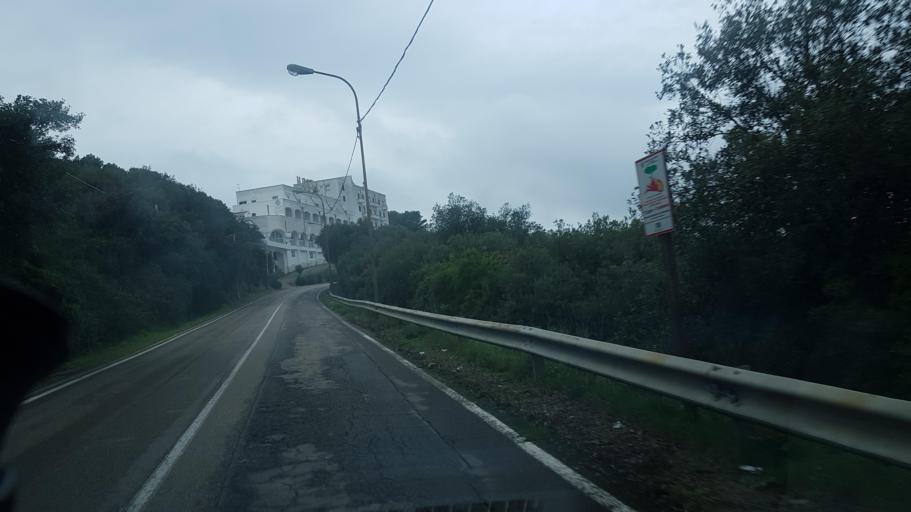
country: IT
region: Apulia
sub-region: Provincia di Brindisi
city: Ostuni
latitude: 40.7318
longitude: 17.5594
